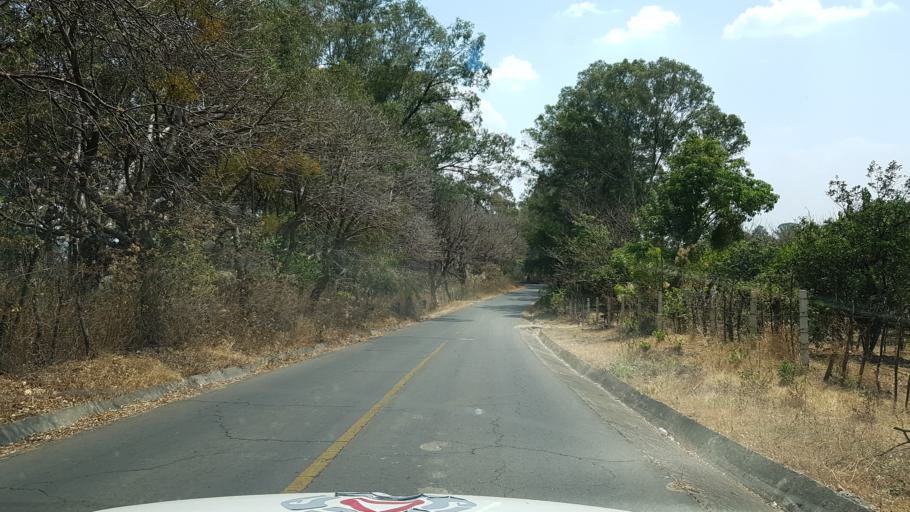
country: MX
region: Morelos
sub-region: Yecapixtla
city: Texcala
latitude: 18.9064
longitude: -98.8081
